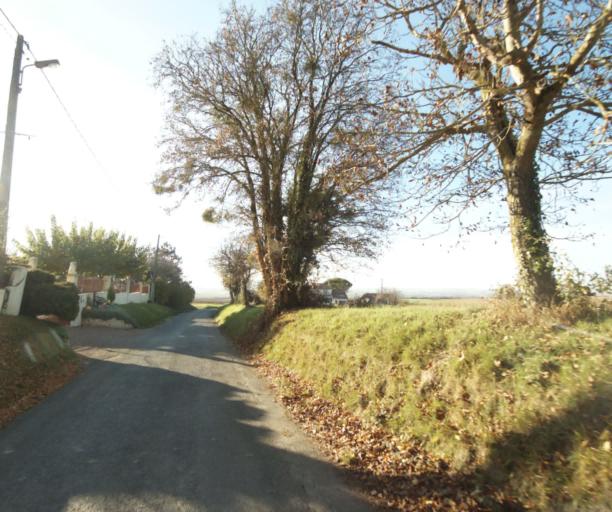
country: FR
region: Poitou-Charentes
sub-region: Departement de la Charente-Maritime
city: Cherac
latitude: 45.7038
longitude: -0.4480
